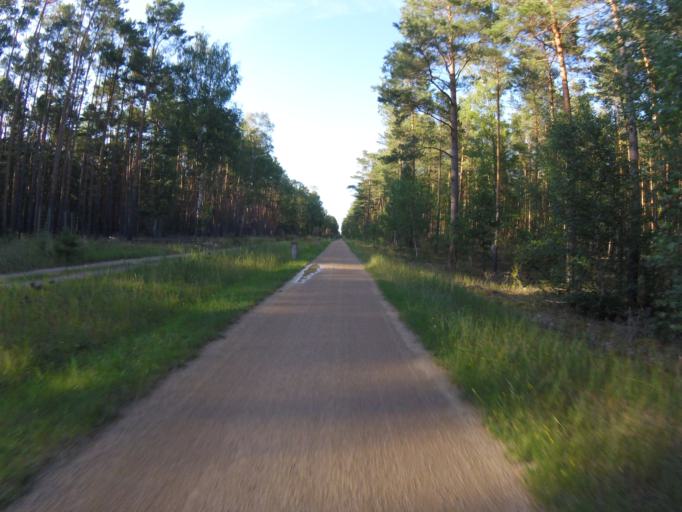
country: DE
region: Brandenburg
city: Halbe
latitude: 52.1881
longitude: 13.7600
